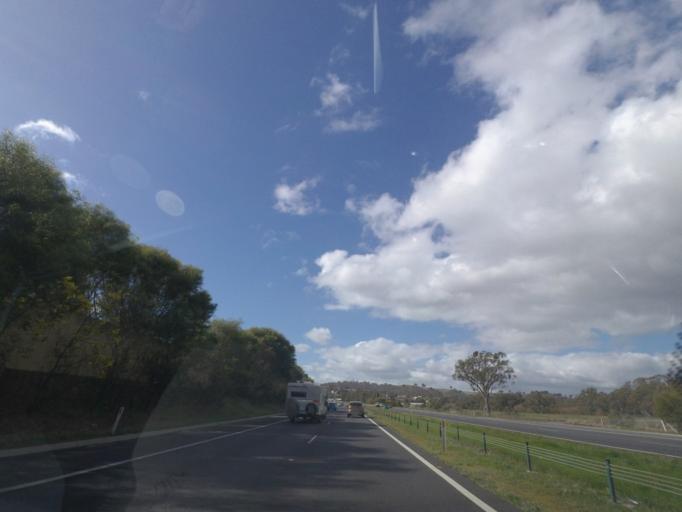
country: AU
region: New South Wales
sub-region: Albury Municipality
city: South Albury
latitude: -36.0971
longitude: 146.9170
